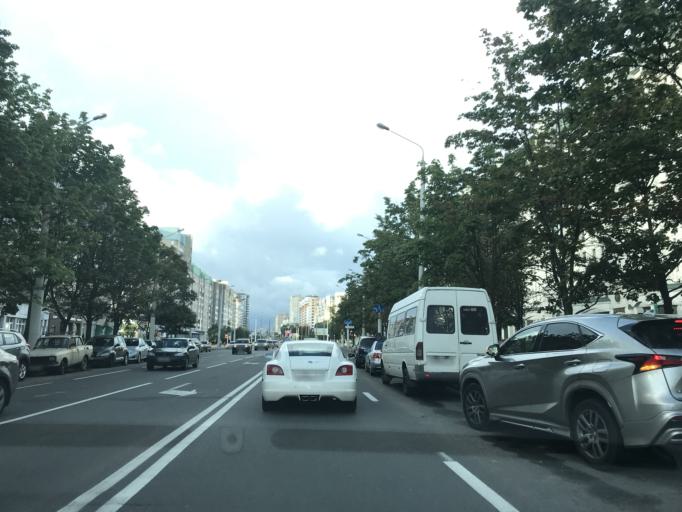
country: BY
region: Minsk
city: Minsk
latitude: 53.9316
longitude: 27.5889
